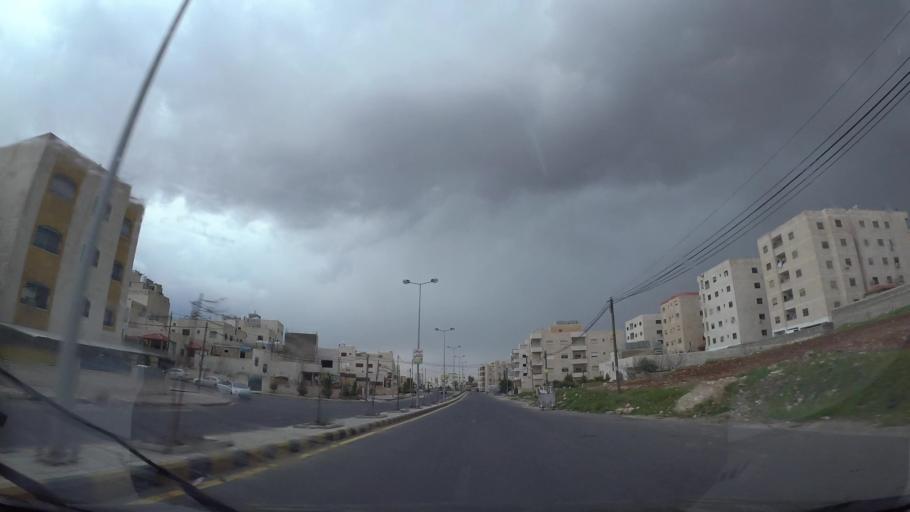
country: JO
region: Amman
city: Amman
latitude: 32.0101
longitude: 35.9593
